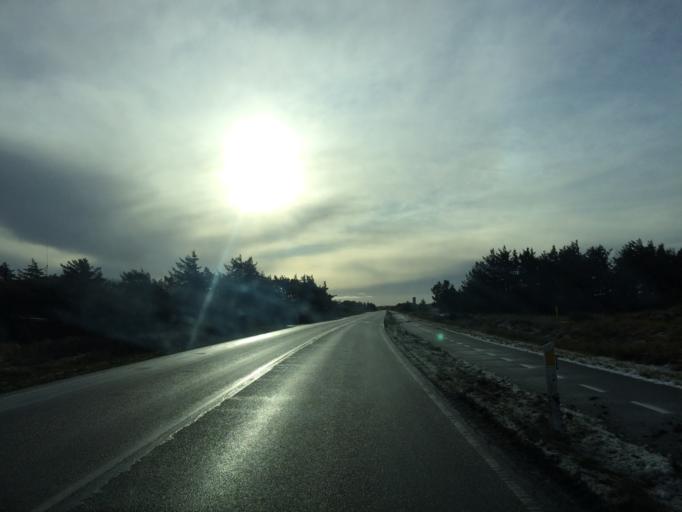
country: DK
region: Central Jutland
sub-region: Ringkobing-Skjern Kommune
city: Hvide Sande
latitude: 56.0628
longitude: 8.1224
